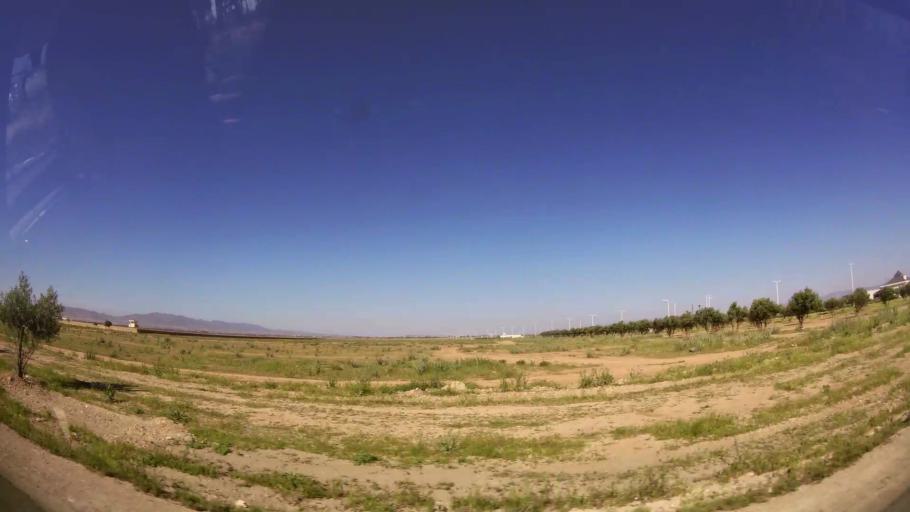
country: MA
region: Oriental
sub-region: Oujda-Angad
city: Oujda
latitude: 34.7731
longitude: -1.9435
